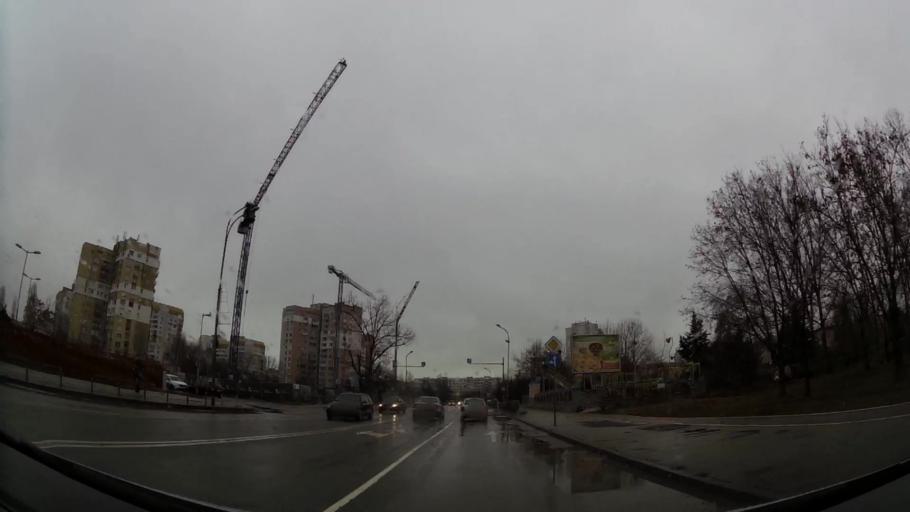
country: BG
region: Sofia-Capital
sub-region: Stolichna Obshtina
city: Sofia
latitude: 42.6432
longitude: 23.3799
